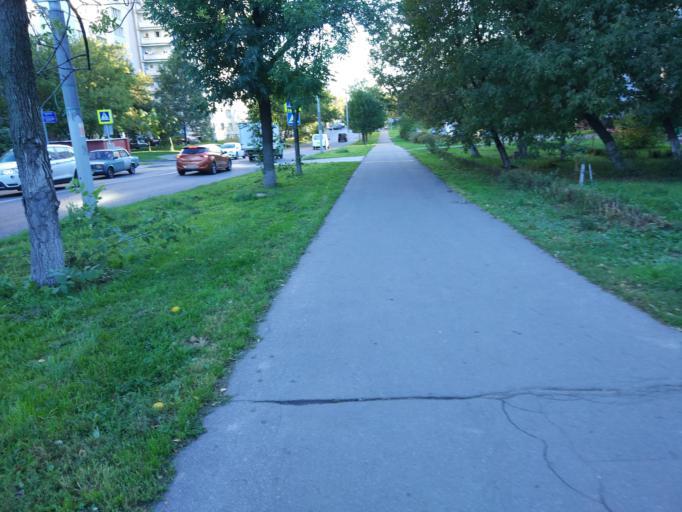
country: RU
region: Moscow
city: Lyublino
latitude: 55.6772
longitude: 37.7273
